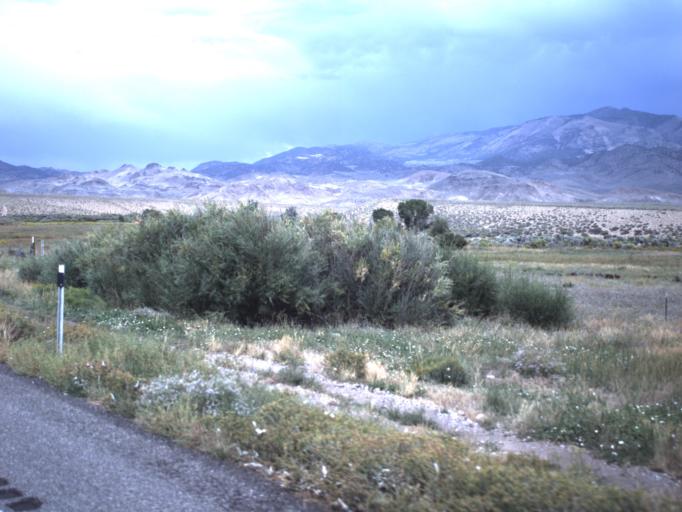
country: US
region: Utah
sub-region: Piute County
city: Junction
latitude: 38.4064
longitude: -112.2312
